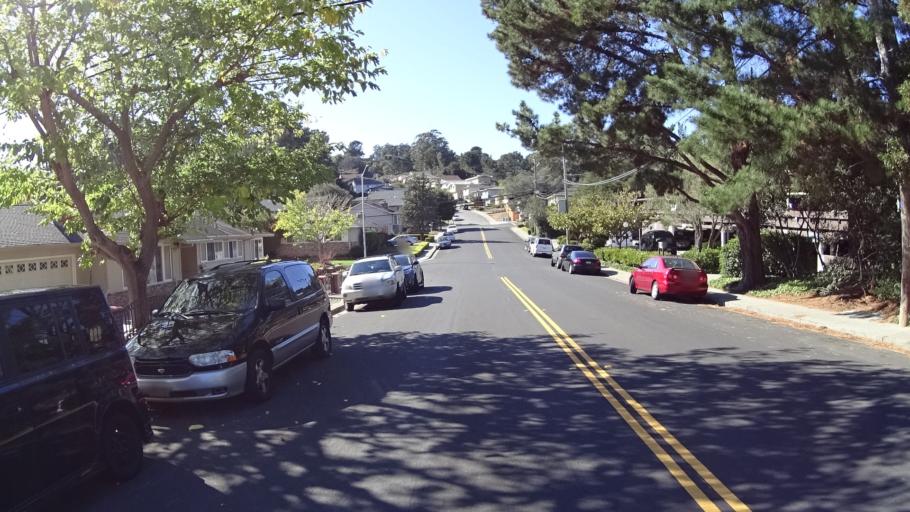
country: US
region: California
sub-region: San Mateo County
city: San Bruno
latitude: 37.6178
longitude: -122.4300
